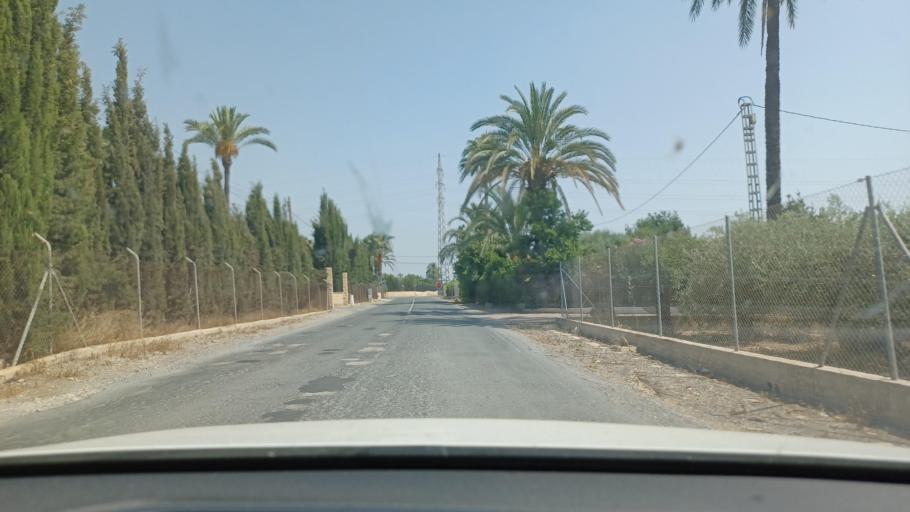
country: ES
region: Valencia
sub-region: Provincia de Alicante
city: Elche
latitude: 38.2285
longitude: -0.6942
